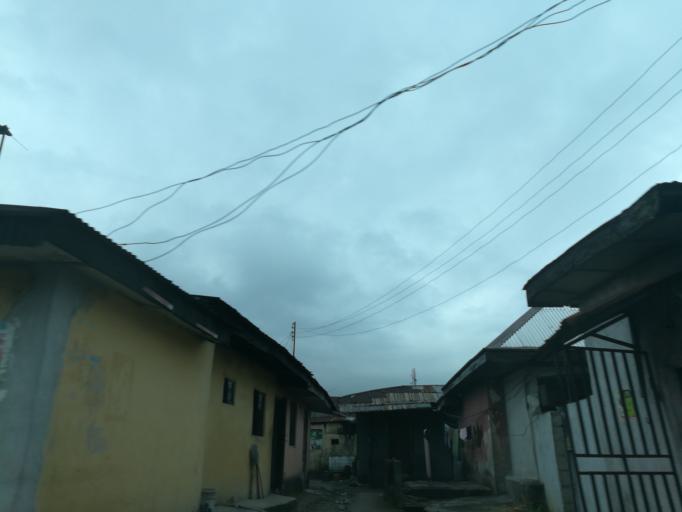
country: NG
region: Rivers
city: Port Harcourt
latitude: 4.8144
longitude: 7.0114
